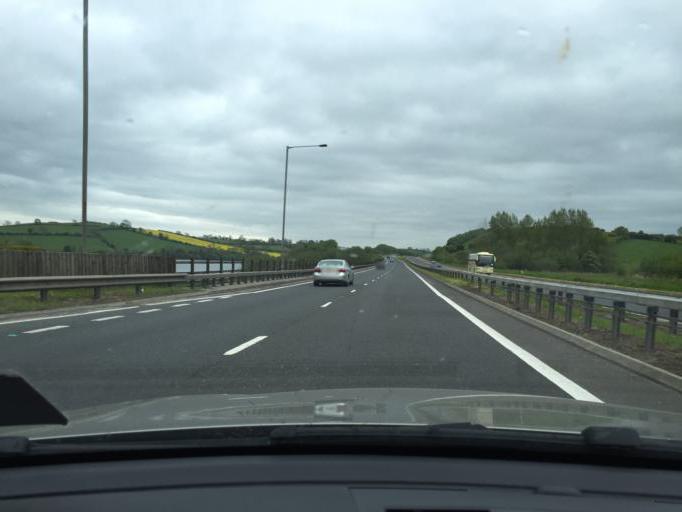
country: GB
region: Northern Ireland
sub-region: Banbridge District
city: Banbridge
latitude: 54.3106
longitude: -6.2988
